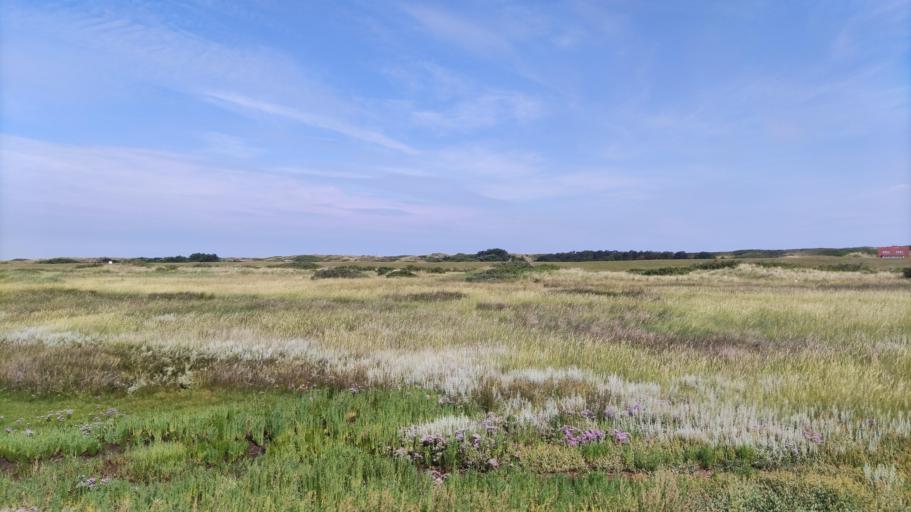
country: DE
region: Lower Saxony
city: Wangerooge
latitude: 53.7892
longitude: 7.8754
